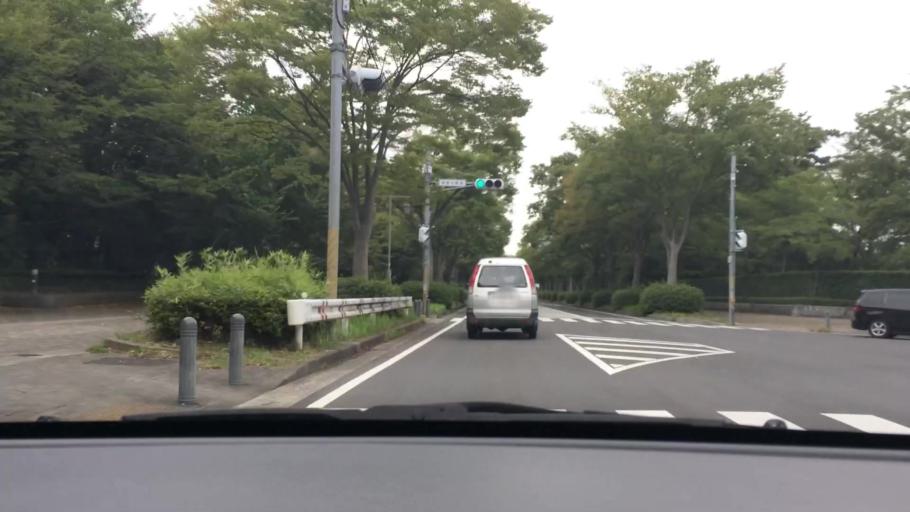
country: JP
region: Chiba
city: Kashiwa
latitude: 35.8959
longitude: 139.9419
